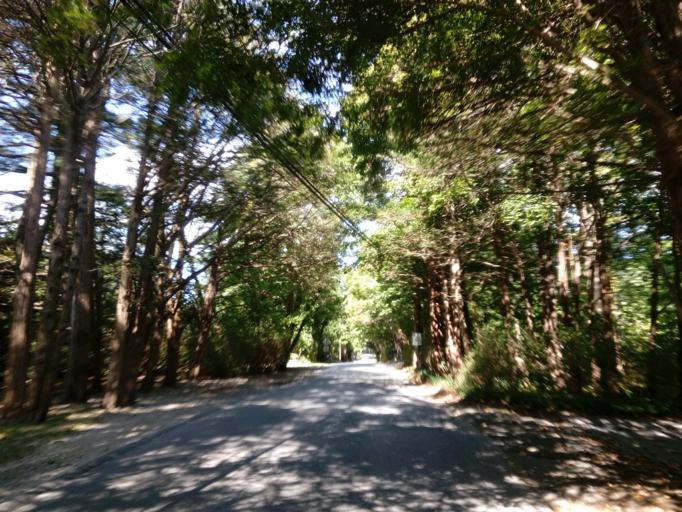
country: US
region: New York
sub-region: Nassau County
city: Laurel Hollow
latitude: 40.8629
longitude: -73.4751
